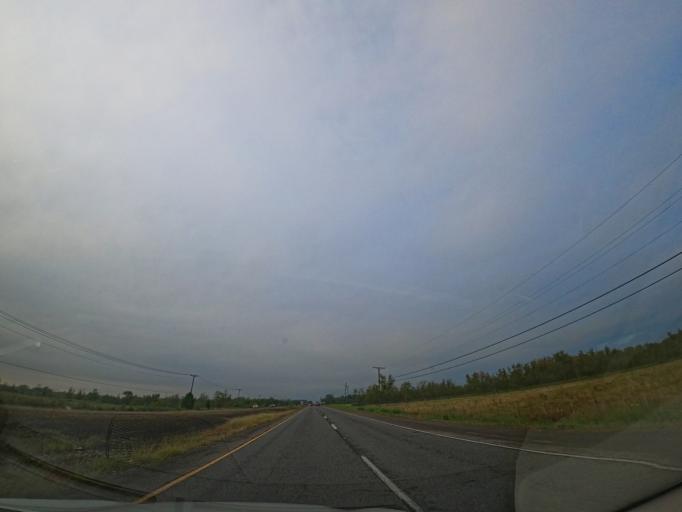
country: US
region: Louisiana
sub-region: Terrebonne Parish
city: Houma
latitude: 29.6584
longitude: -90.6764
